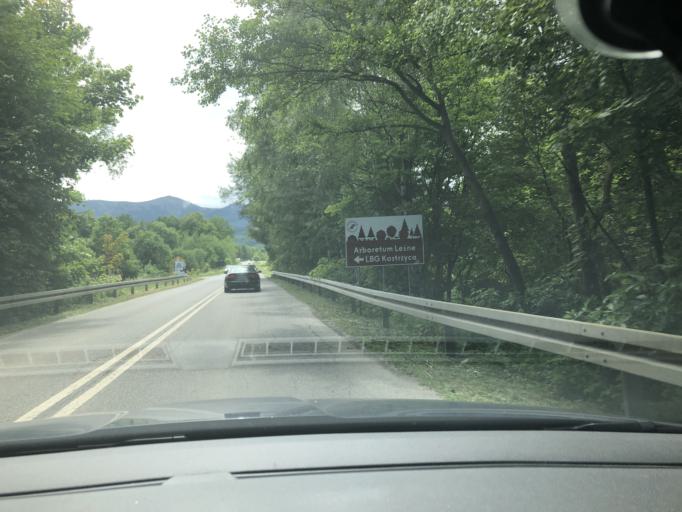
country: PL
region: Lower Silesian Voivodeship
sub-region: Powiat jeleniogorski
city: Myslakowice
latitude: 50.8166
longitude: 15.7720
